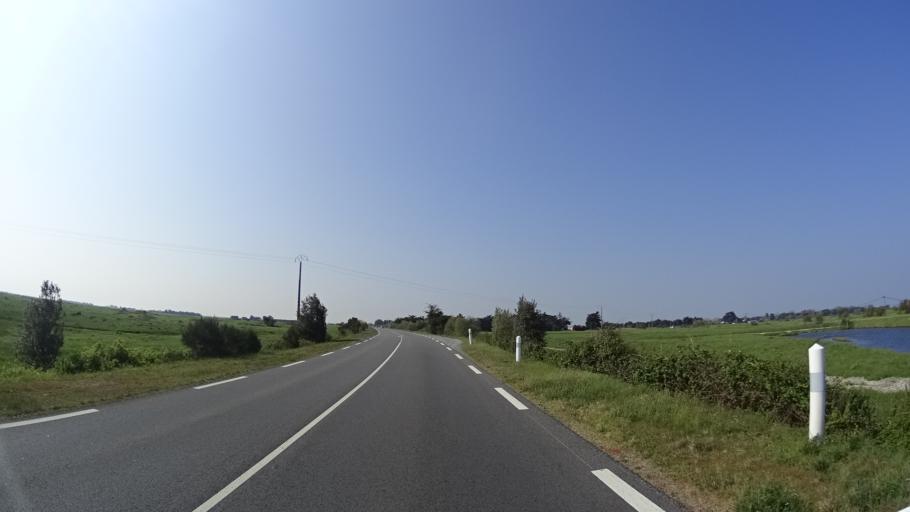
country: FR
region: Pays de la Loire
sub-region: Departement de la Loire-Atlantique
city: Bourgneuf-en-Retz
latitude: 47.0372
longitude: -1.9605
